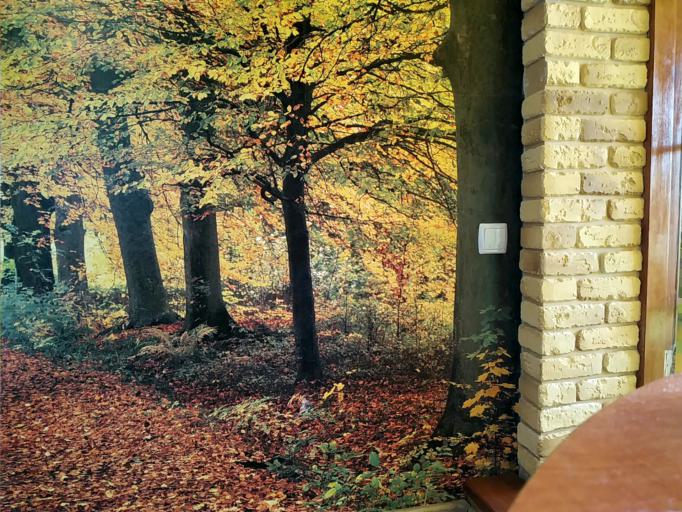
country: RU
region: Novgorod
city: Staraya Russa
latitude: 57.8407
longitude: 31.4524
